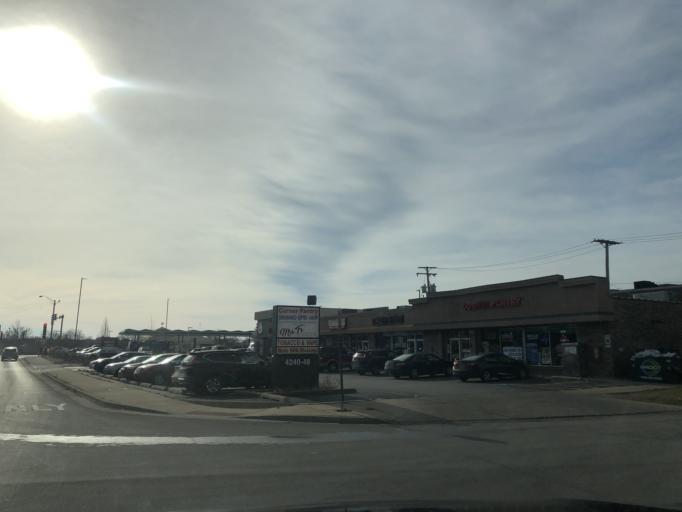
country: US
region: Illinois
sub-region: DuPage County
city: Downers Grove
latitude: 41.8099
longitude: -88.0112
